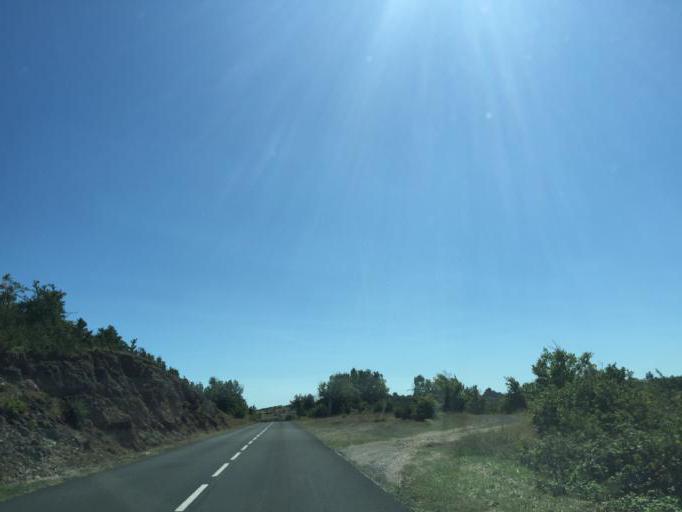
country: FR
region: Languedoc-Roussillon
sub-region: Departement de l'Herault
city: Lodeve
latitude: 43.8908
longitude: 3.3105
